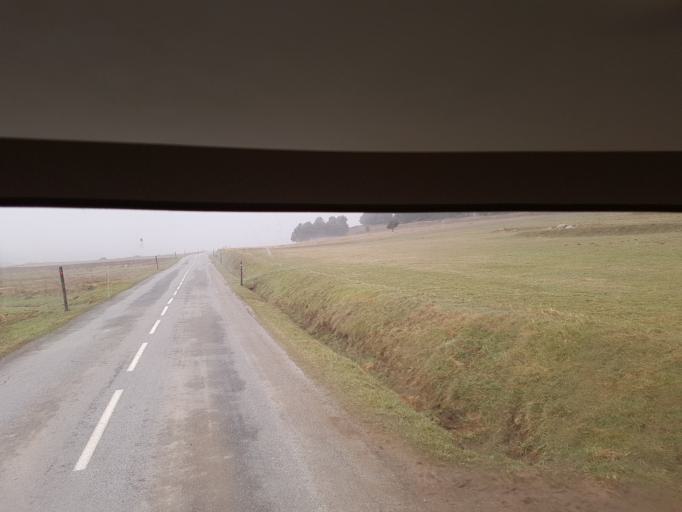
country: ES
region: Catalonia
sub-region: Provincia de Girona
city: Llivia
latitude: 42.5916
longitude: 2.0949
